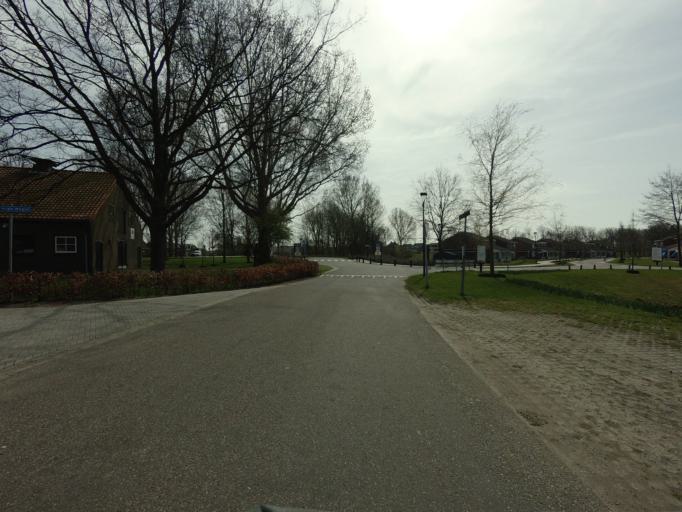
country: NL
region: South Holland
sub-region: Gemeente Den Haag
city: Ypenburg
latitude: 52.0397
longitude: 4.3862
